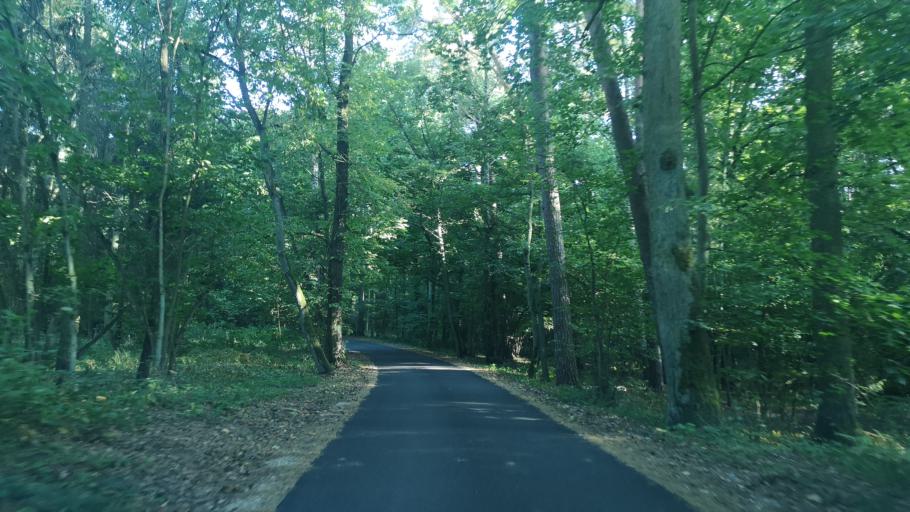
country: PL
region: Kujawsko-Pomorskie
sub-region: Powiat swiecki
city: Warlubie
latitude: 53.4772
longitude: 18.6321
